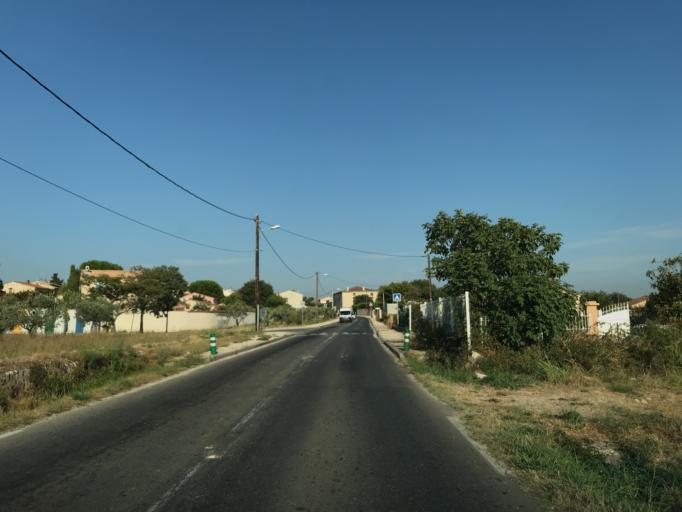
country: FR
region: Provence-Alpes-Cote d'Azur
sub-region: Departement des Bouches-du-Rhone
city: La Fare-les-Oliviers
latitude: 43.5493
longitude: 5.1764
